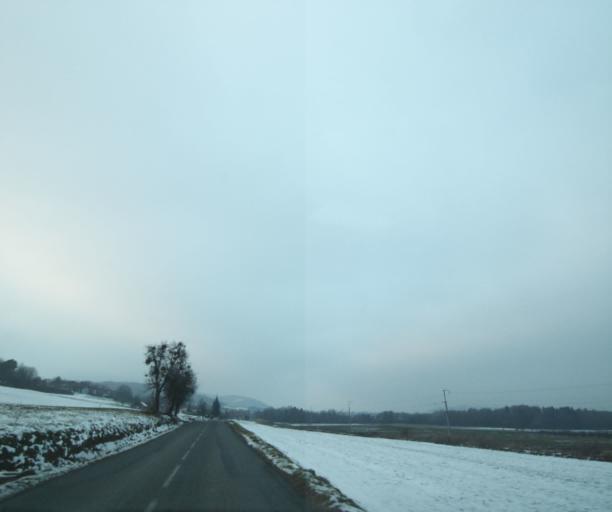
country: FR
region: Rhone-Alpes
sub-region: Departement de la Haute-Savoie
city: Reignier-Esery
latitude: 46.1378
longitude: 6.2553
